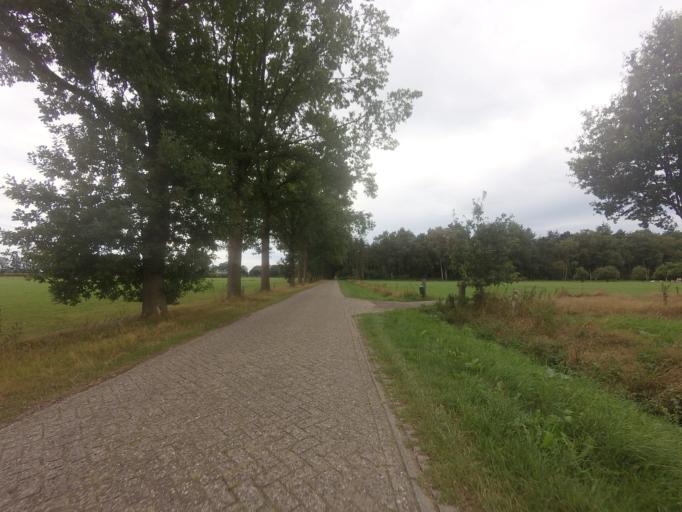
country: NL
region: Overijssel
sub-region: Gemeente Raalte
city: Raalte
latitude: 52.3478
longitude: 6.3264
